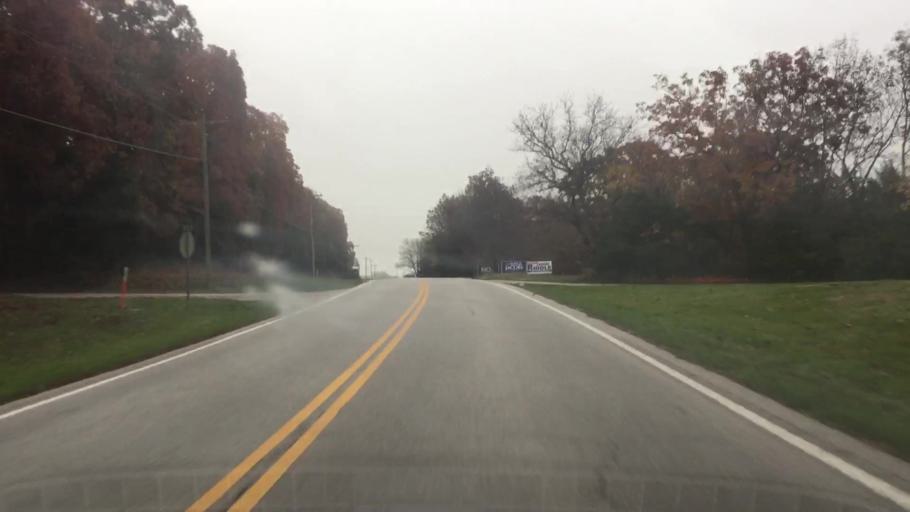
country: US
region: Missouri
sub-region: Callaway County
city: Fulton
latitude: 38.8756
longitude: -92.0713
